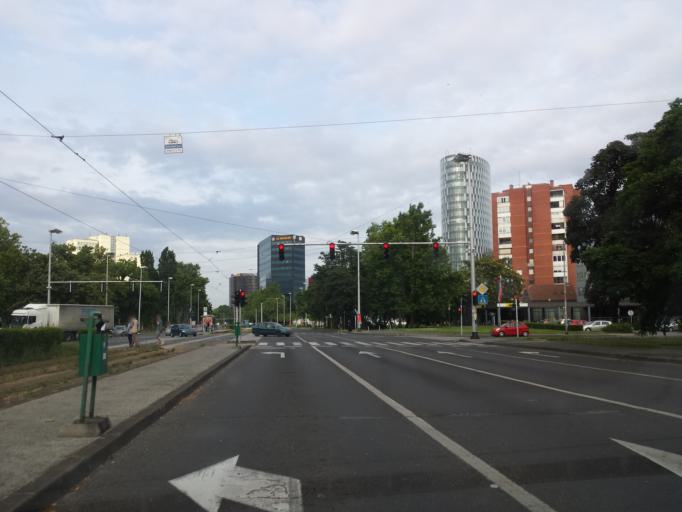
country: HR
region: Grad Zagreb
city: Novi Zagreb
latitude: 45.8014
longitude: 16.0036
